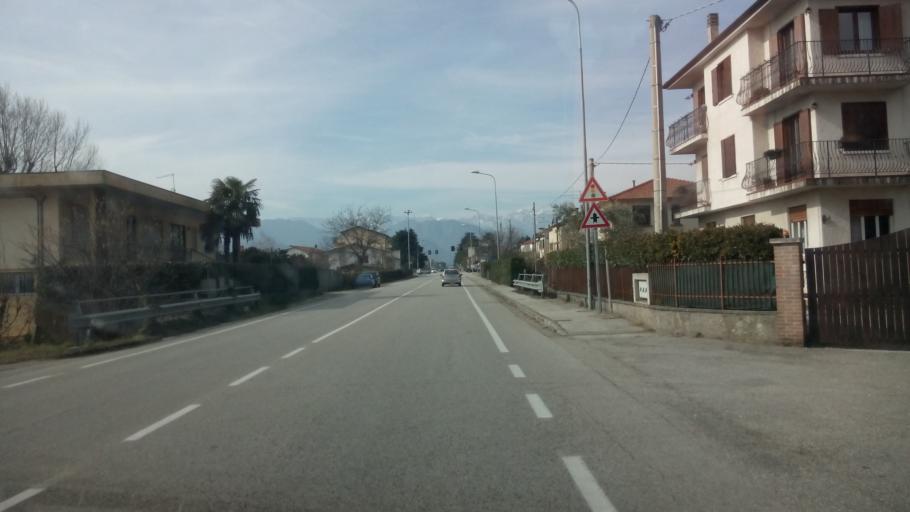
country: IT
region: Veneto
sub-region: Provincia di Vicenza
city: Santorso
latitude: 45.7331
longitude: 11.3894
